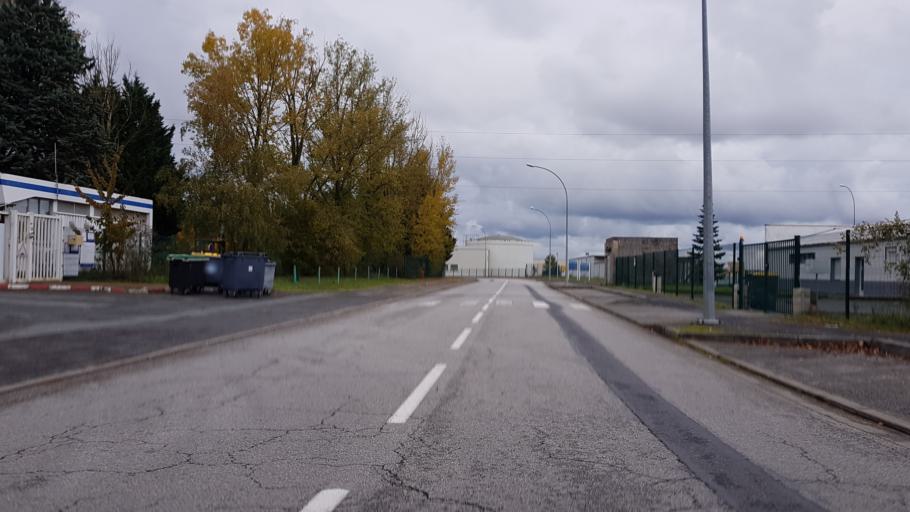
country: FR
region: Poitou-Charentes
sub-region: Departement de la Vienne
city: Chasseneuil-du-Poitou
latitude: 46.6612
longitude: 0.3729
